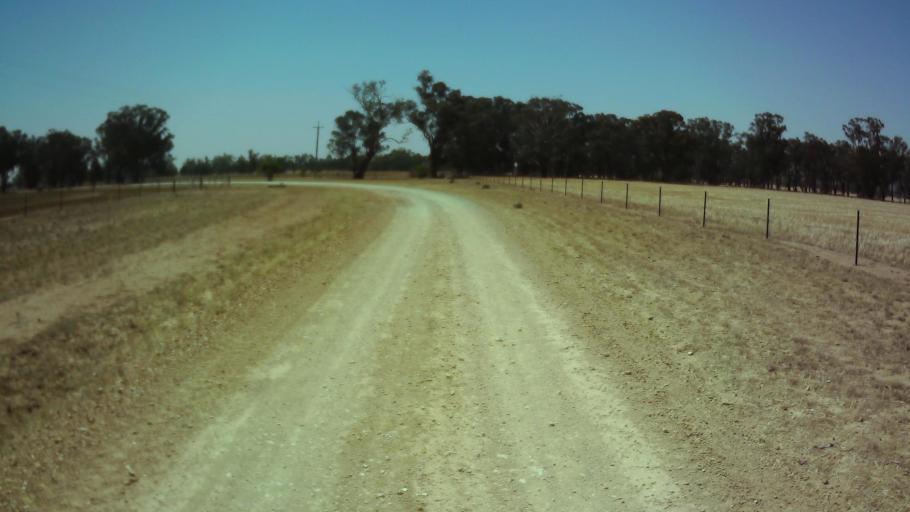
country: AU
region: New South Wales
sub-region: Weddin
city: Grenfell
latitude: -34.0213
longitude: 147.9005
